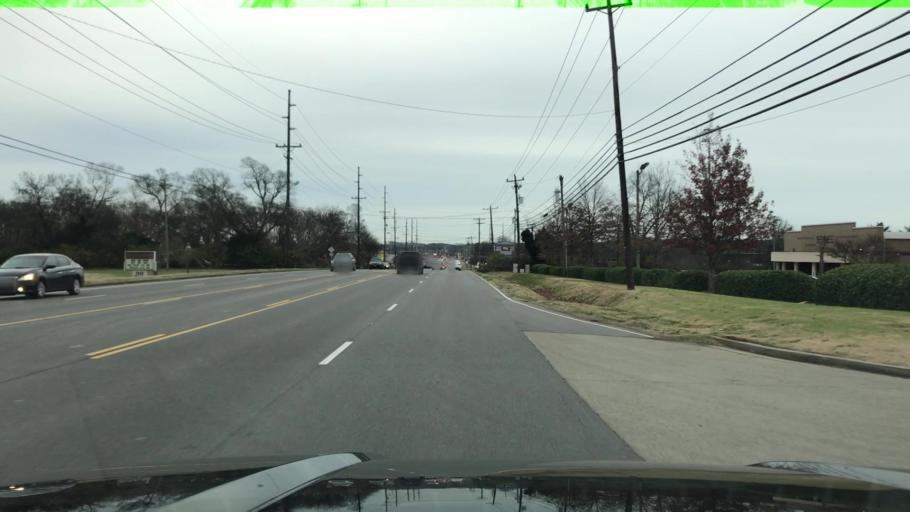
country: US
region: Tennessee
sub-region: Rutherford County
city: La Vergne
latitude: 36.0315
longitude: -86.5941
